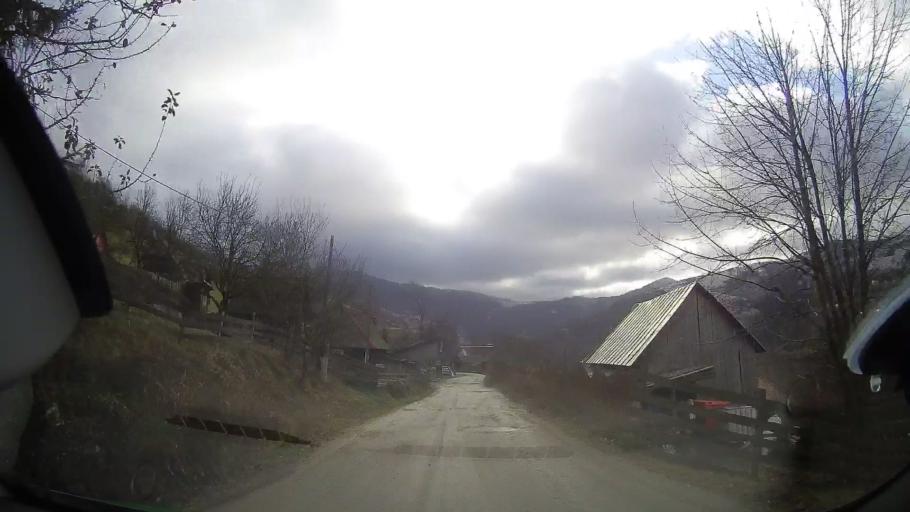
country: RO
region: Cluj
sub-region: Comuna Valea Ierii
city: Valea Ierii
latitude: 46.6795
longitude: 23.3103
